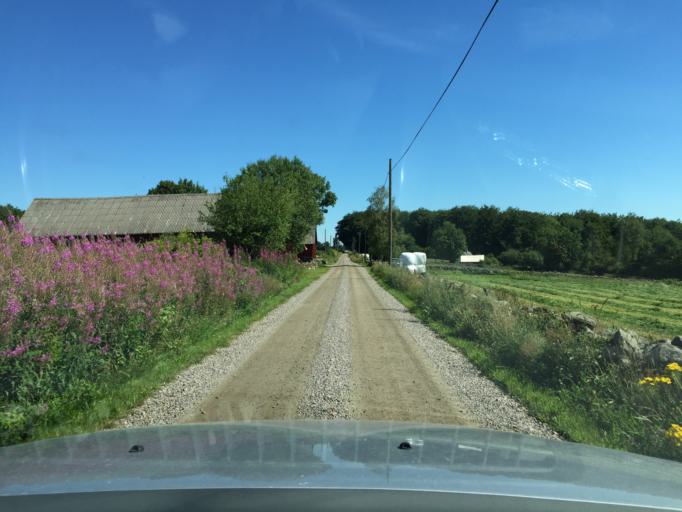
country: SE
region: Skane
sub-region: Hassleholms Kommun
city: Sosdala
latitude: 56.0155
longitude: 13.6356
